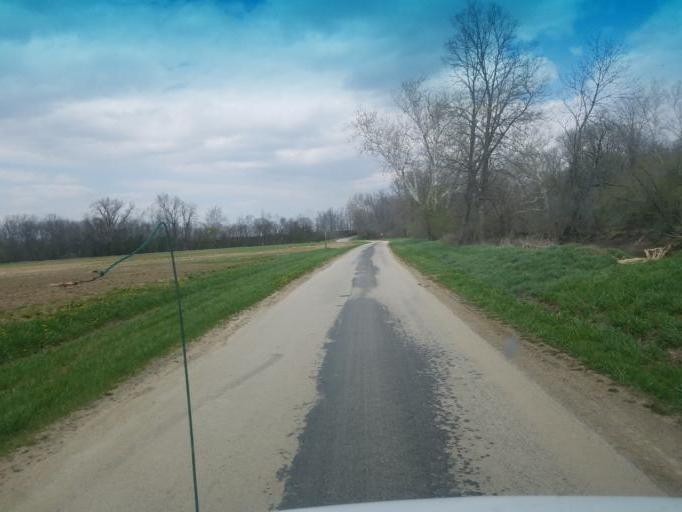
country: US
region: Ohio
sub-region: Wyandot County
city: Upper Sandusky
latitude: 40.9252
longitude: -83.2476
